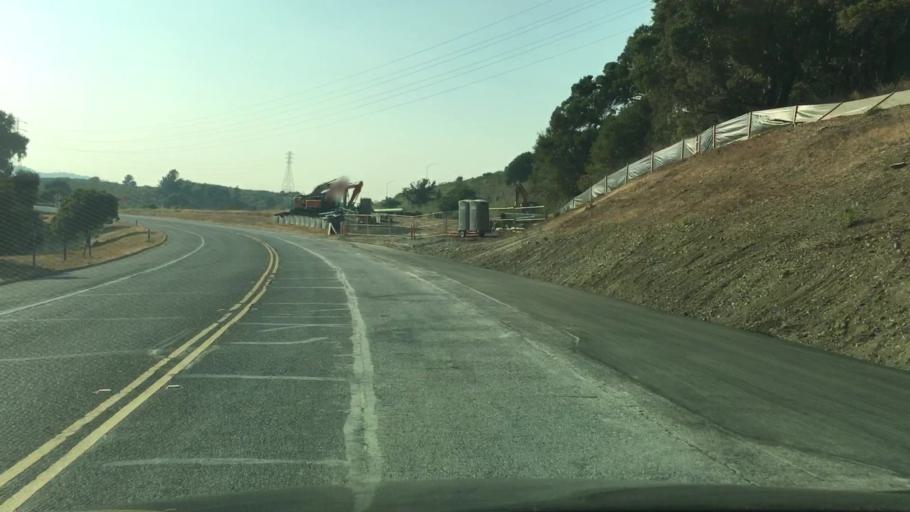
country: US
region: California
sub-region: San Mateo County
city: Highlands-Baywood Park
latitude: 37.4991
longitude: -122.3285
